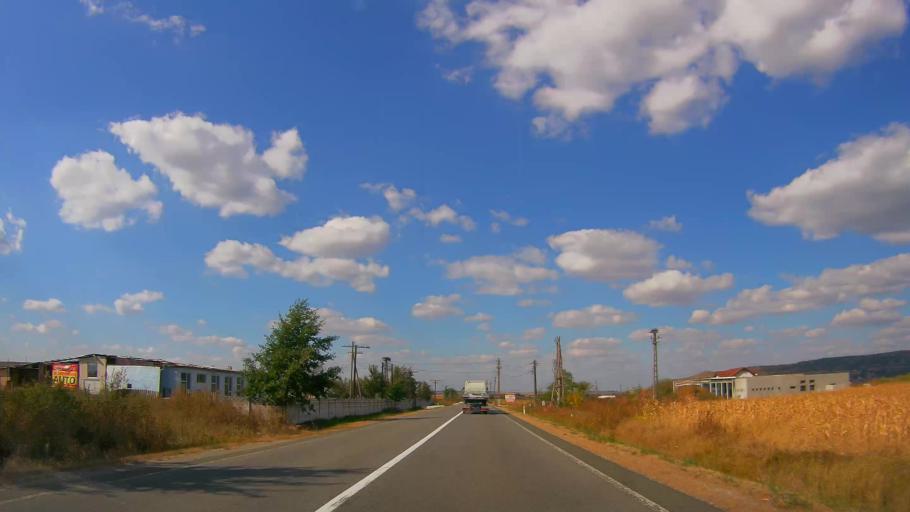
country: RO
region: Salaj
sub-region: Comuna Bobota
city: Dersida
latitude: 47.3643
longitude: 22.7928
